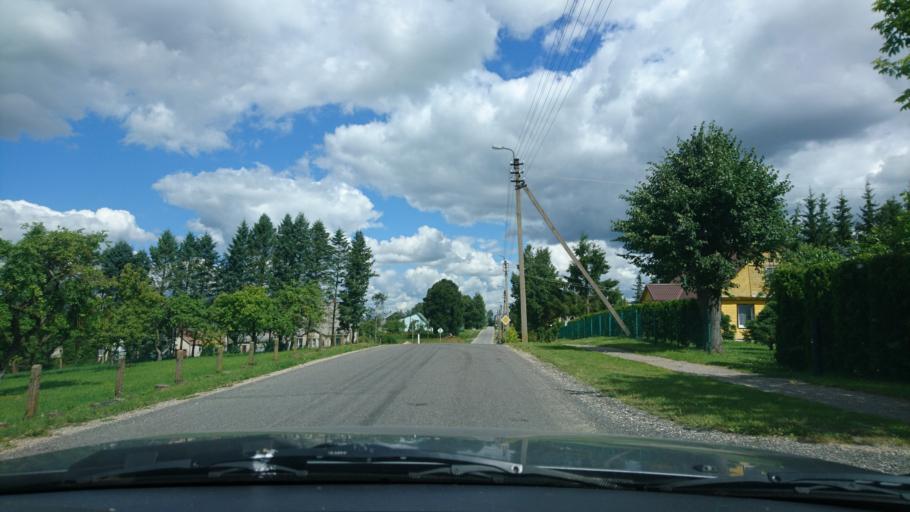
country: LT
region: Panevezys
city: Rokiskis
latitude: 55.9478
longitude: 25.7987
